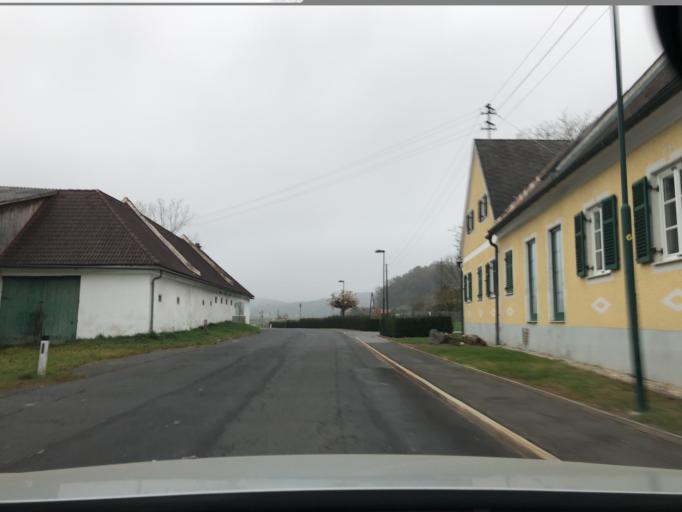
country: AT
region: Styria
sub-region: Politischer Bezirk Suedoststeiermark
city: Fehring
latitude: 46.9558
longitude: 16.0352
